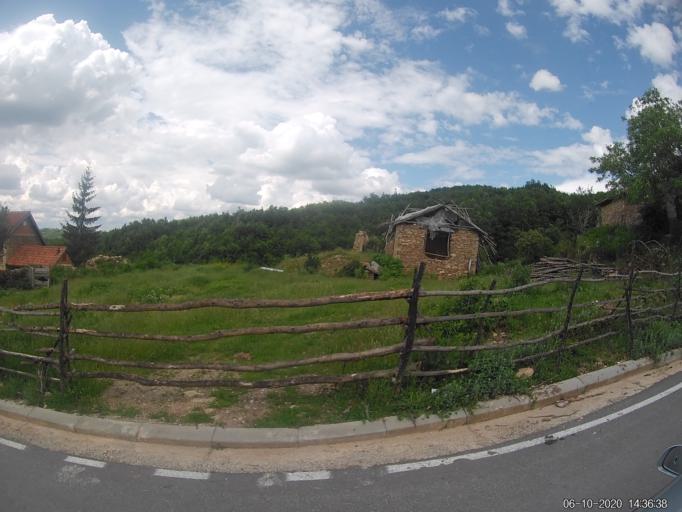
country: XK
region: Prizren
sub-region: Komuna e Therandes
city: Budakovo
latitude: 42.4099
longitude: 20.9370
